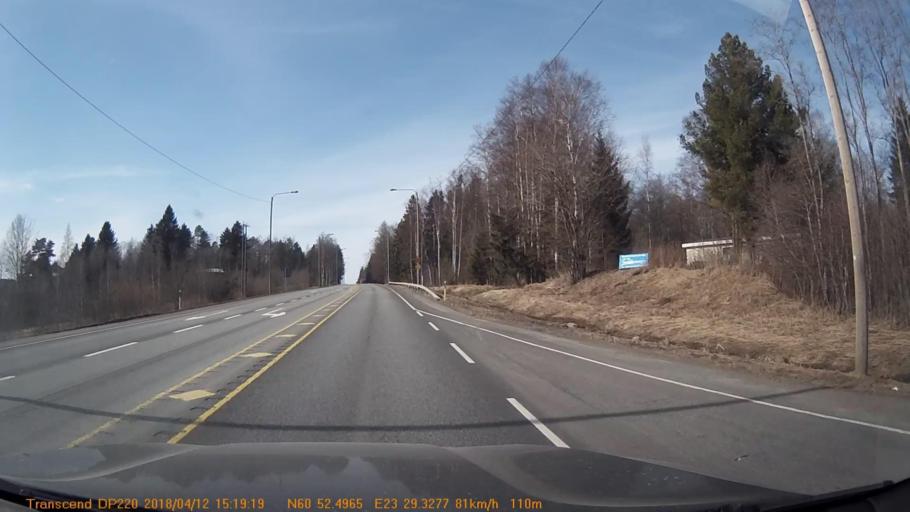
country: FI
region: Haeme
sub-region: Forssa
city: Jokioinen
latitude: 60.8752
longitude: 23.4883
